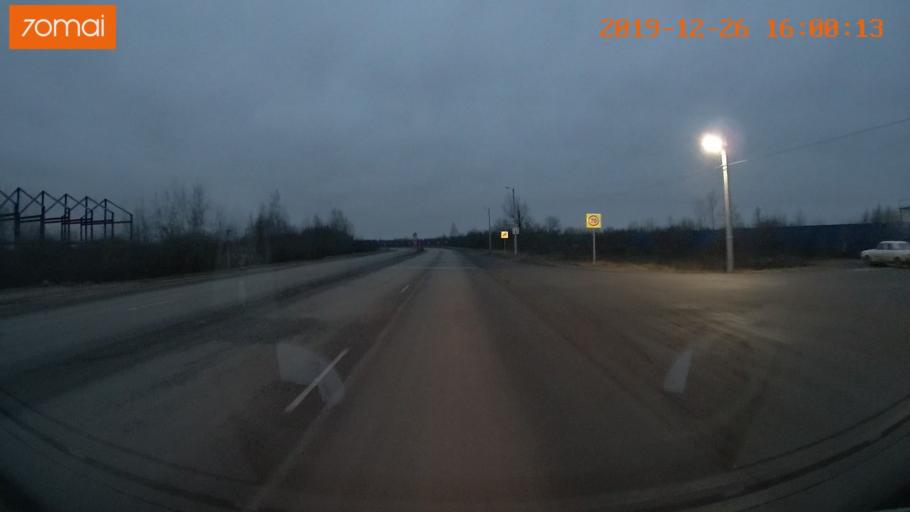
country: RU
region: Jaroslavl
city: Rybinsk
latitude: 58.0266
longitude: 38.8031
